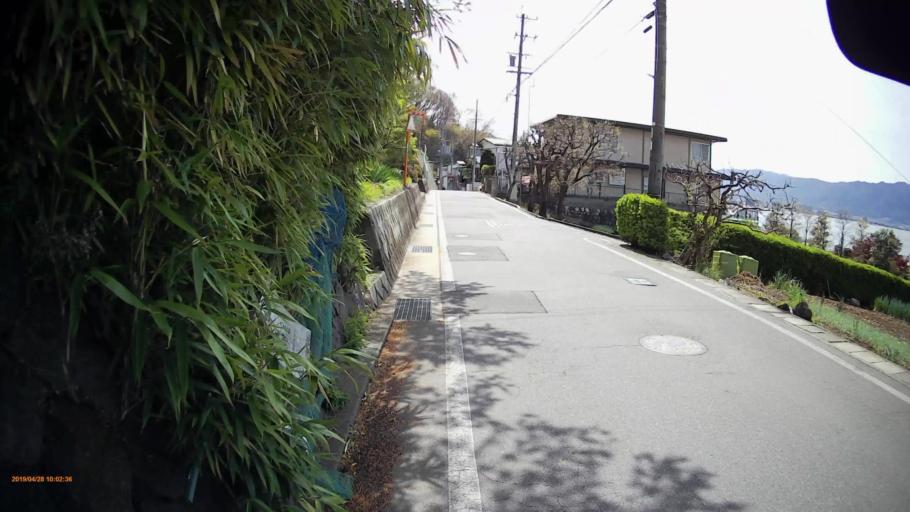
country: JP
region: Nagano
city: Suwa
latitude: 36.0695
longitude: 138.0988
